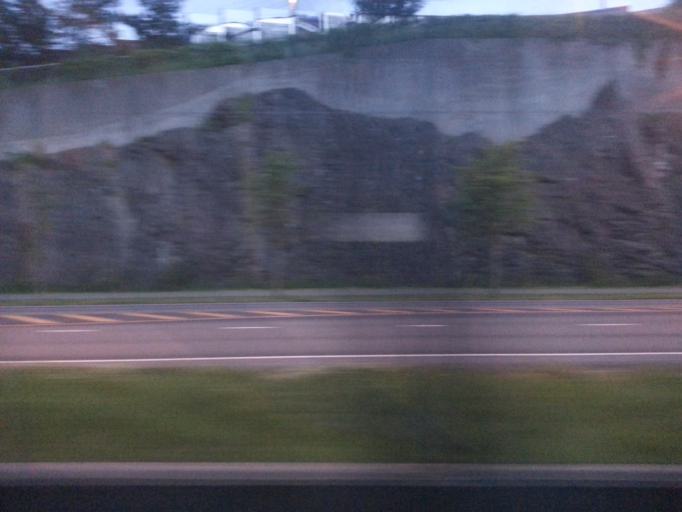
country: NO
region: Akershus
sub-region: Skedsmo
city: Lillestrom
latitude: 59.9523
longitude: 11.0304
